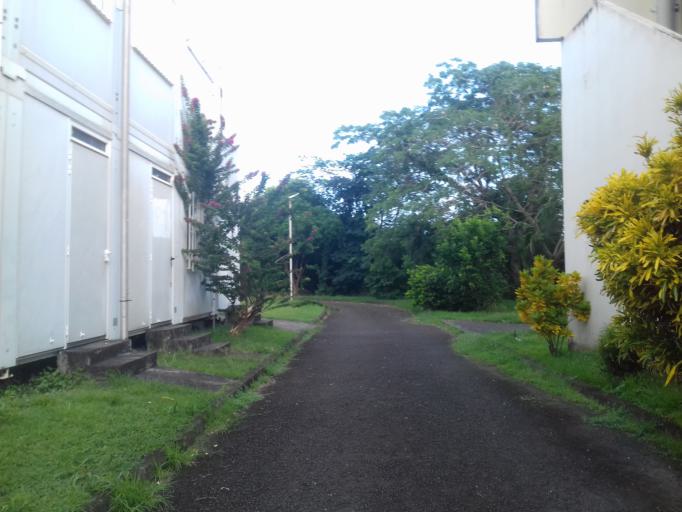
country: MQ
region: Martinique
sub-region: Martinique
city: Fort-de-France
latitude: 14.6191
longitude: -61.0935
